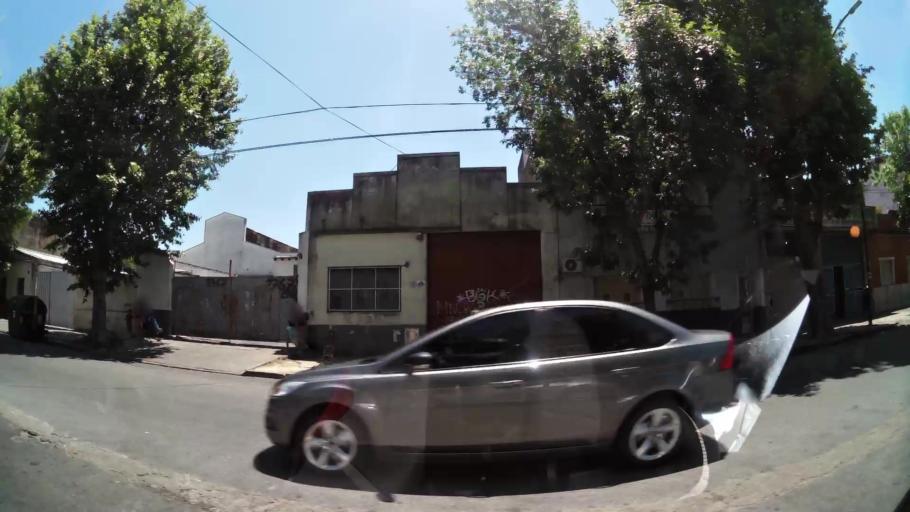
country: AR
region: Buenos Aires
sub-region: Partido de Avellaneda
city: Avellaneda
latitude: -34.6504
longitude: -58.3847
